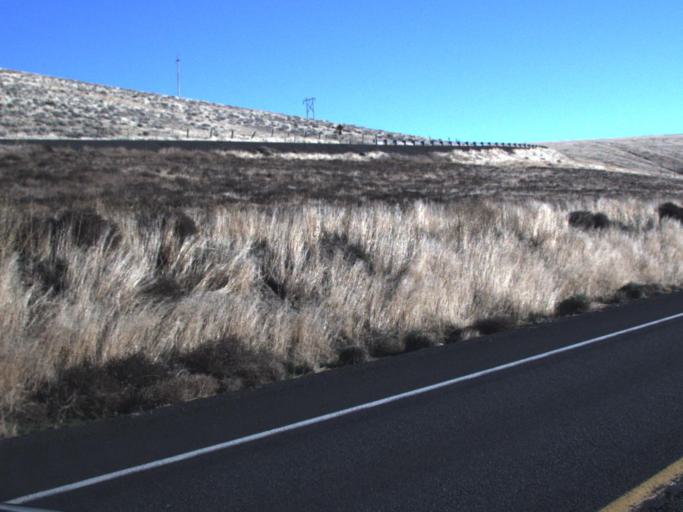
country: US
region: Washington
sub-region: Garfield County
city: Pomeroy
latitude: 46.4724
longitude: -117.5292
